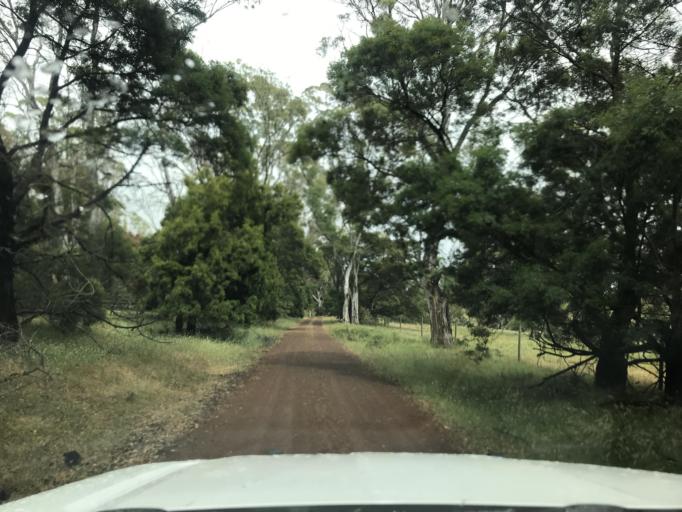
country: AU
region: South Australia
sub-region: Wattle Range
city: Penola
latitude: -37.2639
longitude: 141.3216
